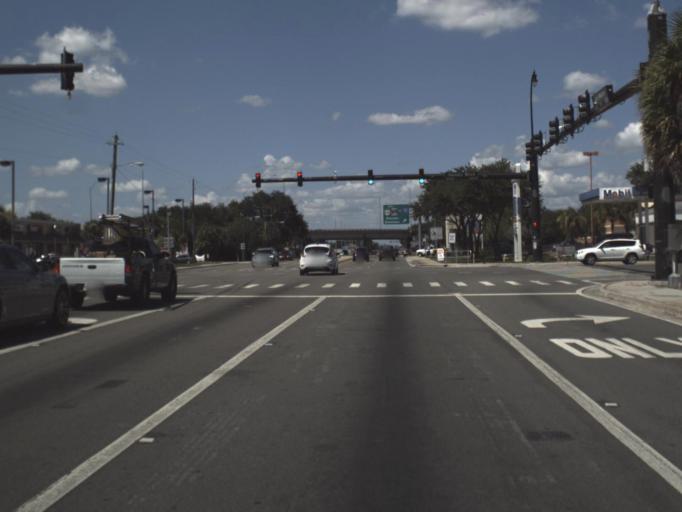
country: US
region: Florida
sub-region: Hillsborough County
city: Tampa
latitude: 27.8933
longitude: -82.5063
